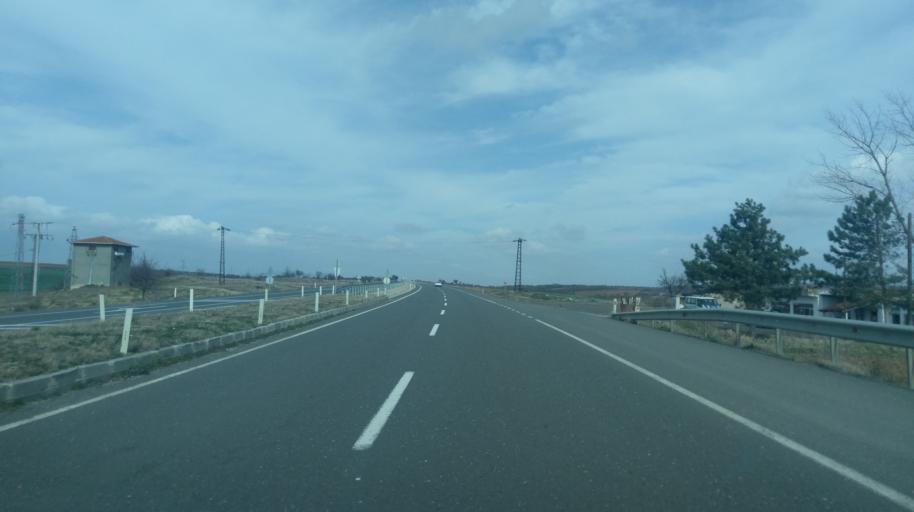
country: TR
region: Edirne
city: Hamidiye
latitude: 41.1150
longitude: 26.6507
